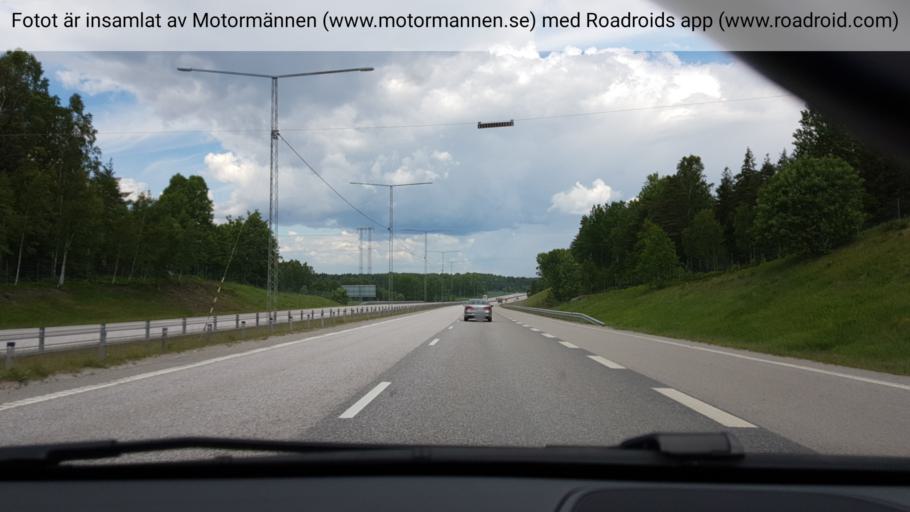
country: SE
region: Stockholm
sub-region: Haninge Kommun
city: Jordbro
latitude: 59.1126
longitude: 18.1271
